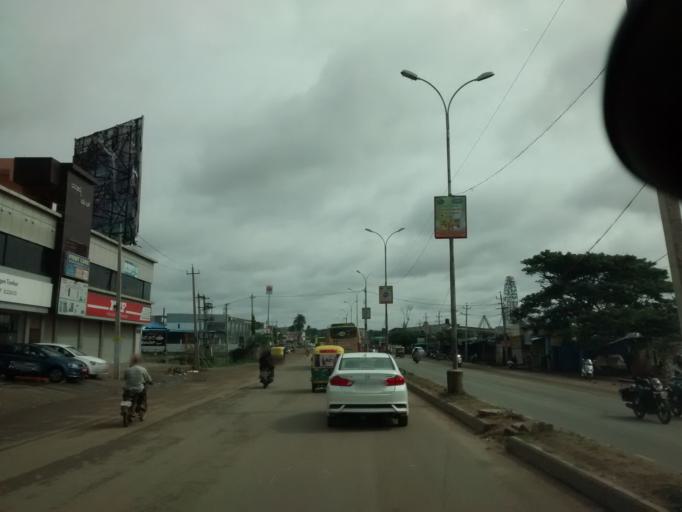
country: IN
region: Karnataka
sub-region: Tumkur
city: Tumkur
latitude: 13.3528
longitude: 77.1033
